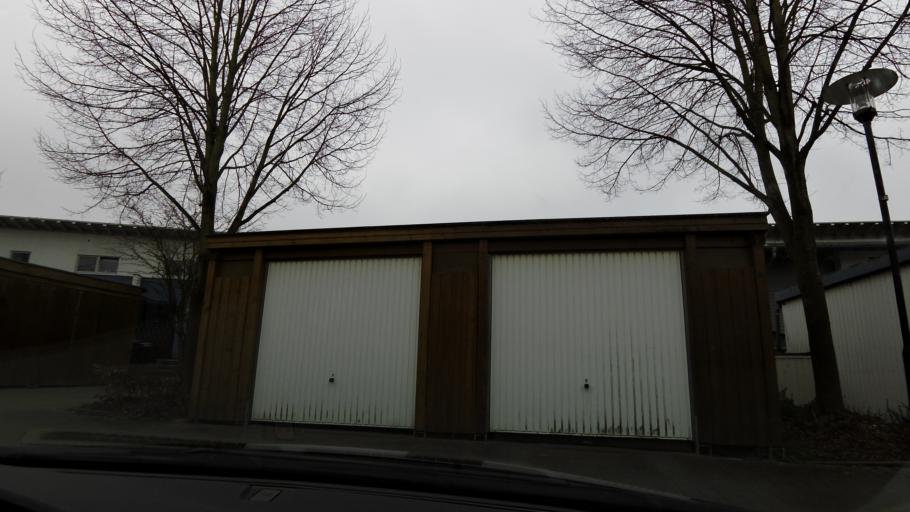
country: DE
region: North Rhine-Westphalia
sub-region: Regierungsbezirk Koln
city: Ubach-Palenberg
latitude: 50.9193
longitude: 6.1022
